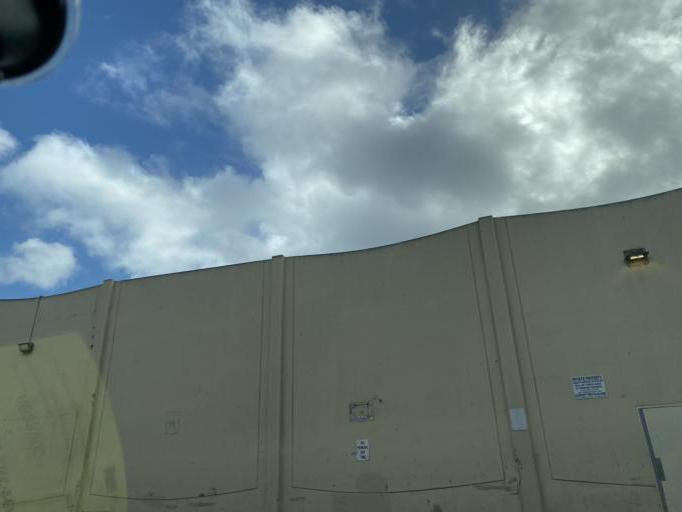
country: US
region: California
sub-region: San Francisco County
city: San Francisco
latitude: 37.7670
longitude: -122.4089
